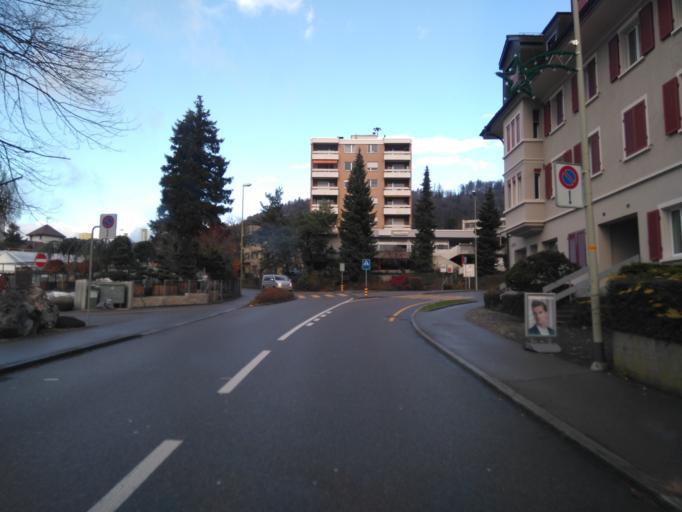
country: CH
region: Zurich
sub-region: Bezirk Dietikon
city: Unterengstringen
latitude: 47.4124
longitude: 8.4493
